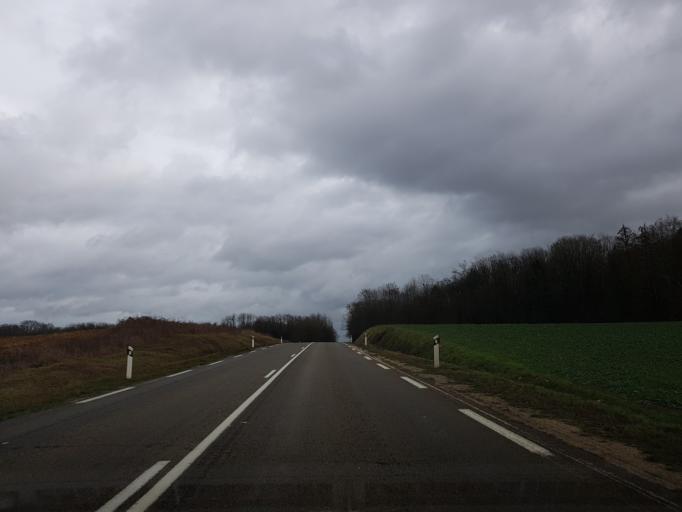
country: FR
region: Franche-Comte
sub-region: Departement de la Haute-Saone
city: Jussey
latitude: 47.7204
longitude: 5.8613
